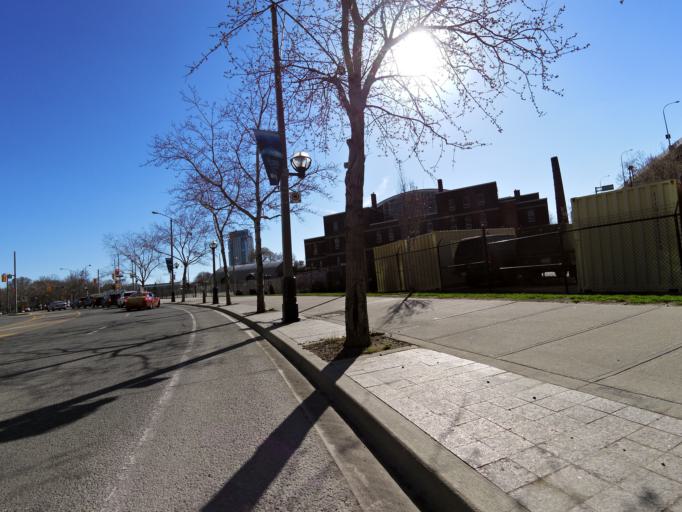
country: CA
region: Ontario
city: Toronto
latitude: 43.6372
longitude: -79.4066
